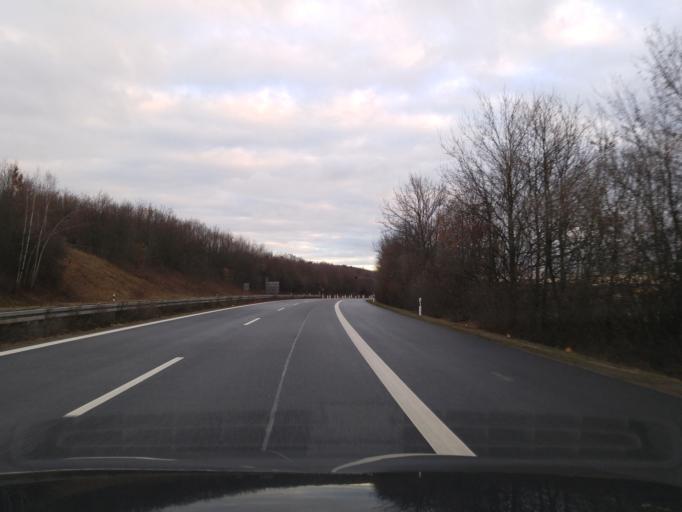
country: DE
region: Saxony
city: Dennheritz
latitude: 50.7926
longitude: 12.4778
